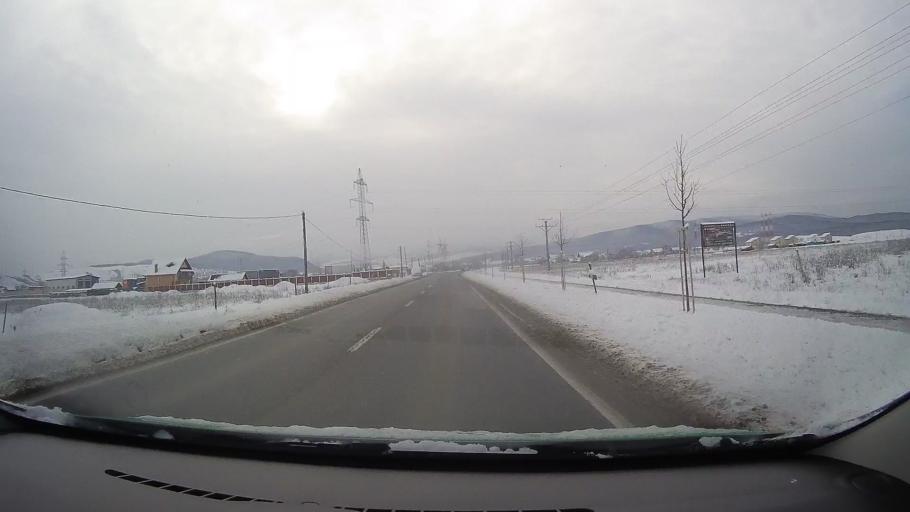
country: RO
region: Alba
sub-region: Municipiul Sebes
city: Petresti
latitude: 45.9350
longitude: 23.5617
